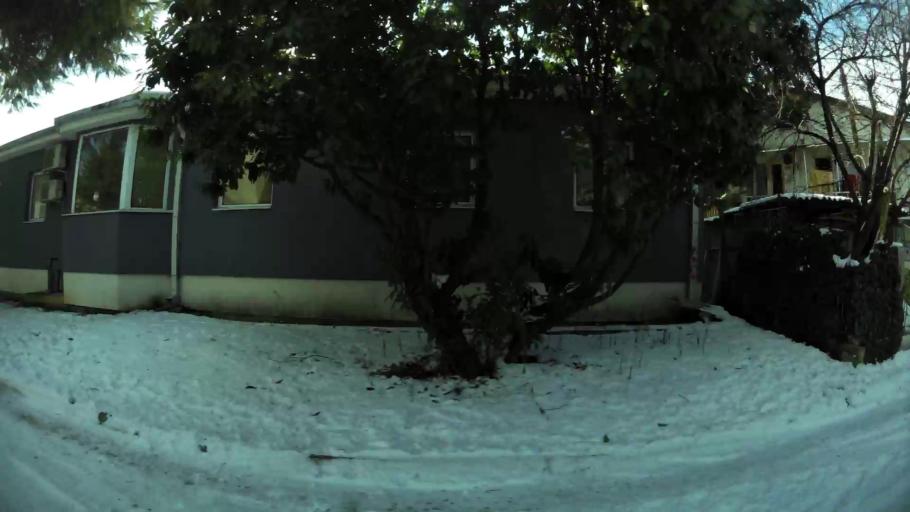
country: MK
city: Krushopek
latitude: 42.0028
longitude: 21.3648
